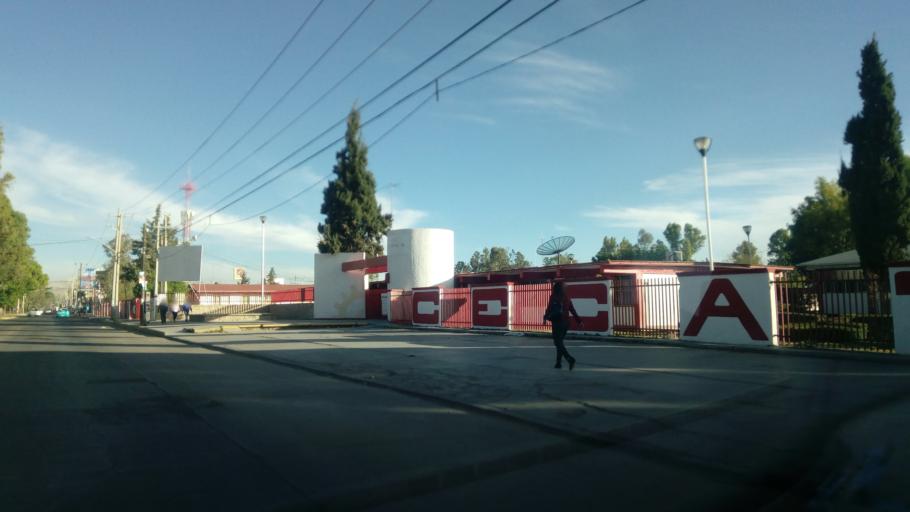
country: MX
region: Durango
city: Victoria de Durango
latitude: 24.0598
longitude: -104.6002
